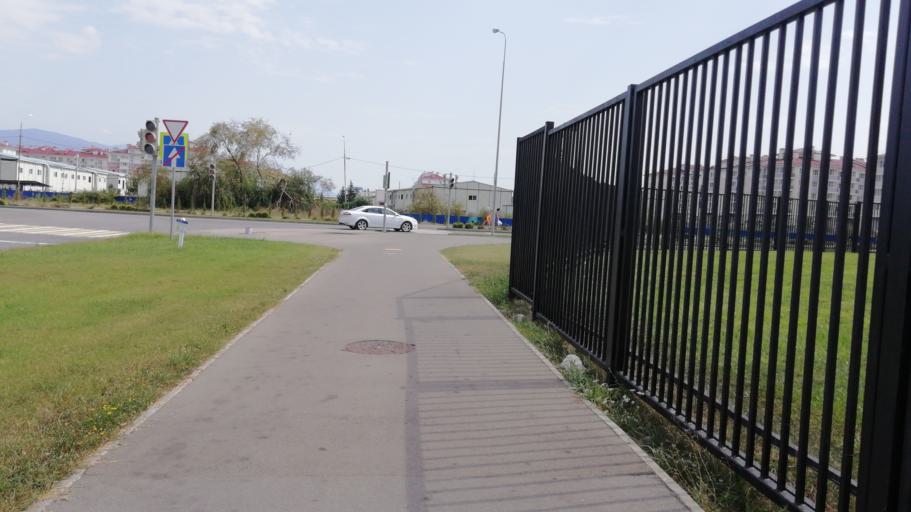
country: RU
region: Krasnodarskiy
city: Vysokoye
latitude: 43.4037
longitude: 39.9791
